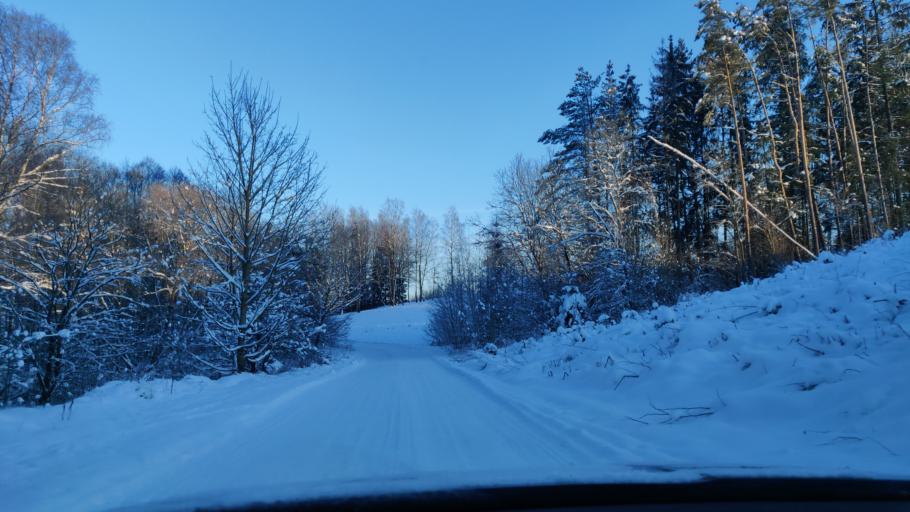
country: LT
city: Trakai
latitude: 54.6134
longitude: 24.9318
